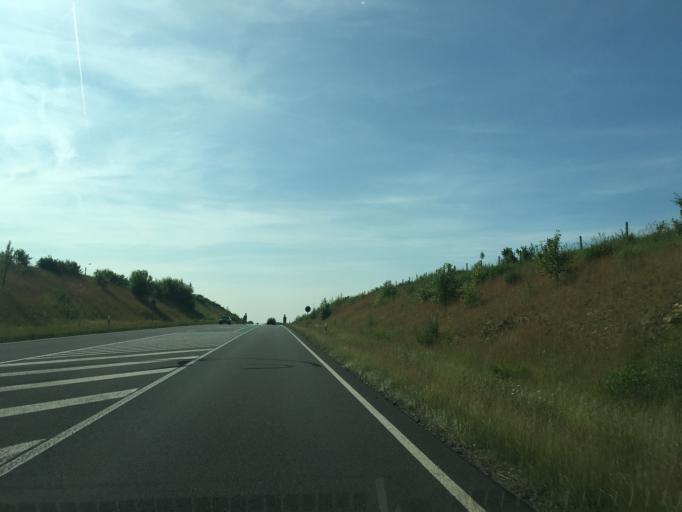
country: DE
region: North Rhine-Westphalia
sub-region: Regierungsbezirk Munster
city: Steinfurt
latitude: 52.1643
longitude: 7.3090
